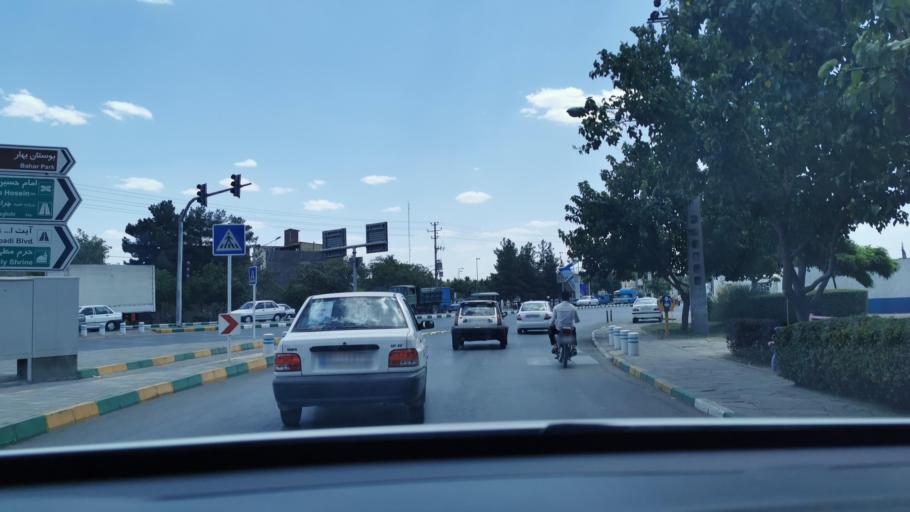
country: IR
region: Razavi Khorasan
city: Mashhad
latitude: 36.3377
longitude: 59.6258
